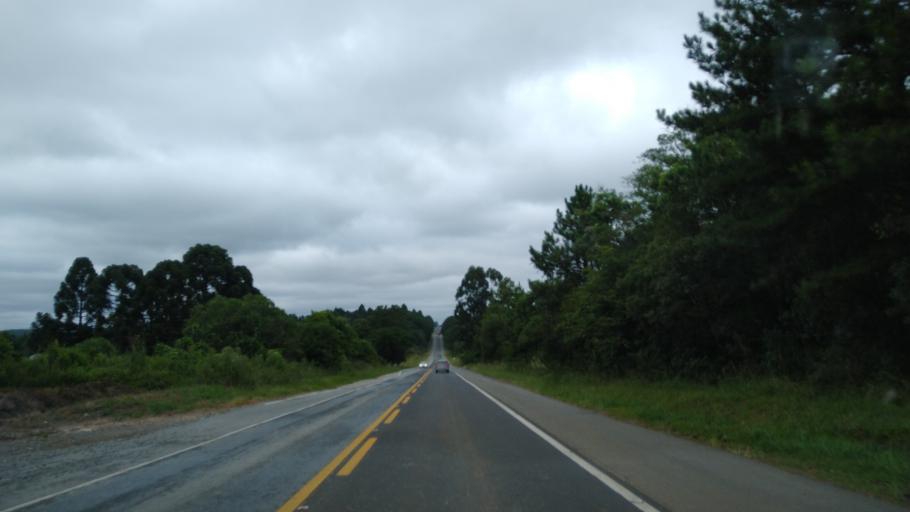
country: BR
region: Santa Catarina
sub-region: Tres Barras
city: Tres Barras
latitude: -26.1749
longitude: -50.1720
